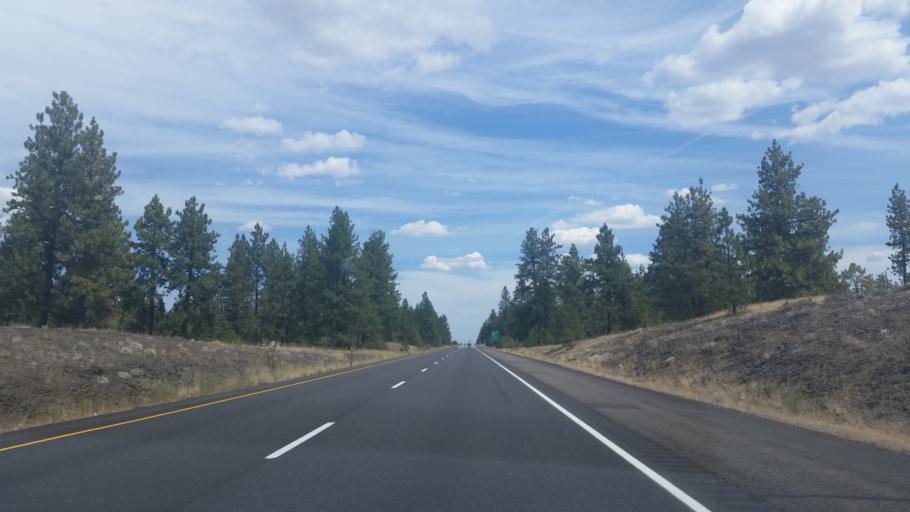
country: US
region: Washington
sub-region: Spokane County
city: Medical Lake
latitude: 47.4206
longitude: -117.8093
